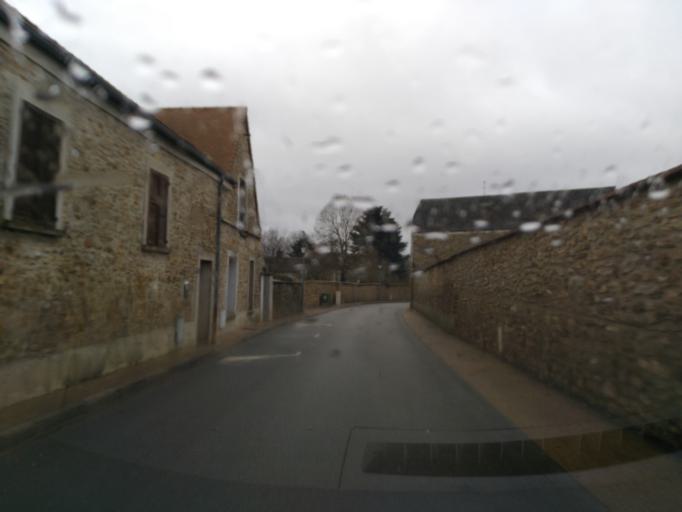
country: FR
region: Ile-de-France
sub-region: Departement des Yvelines
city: Thoiry
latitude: 48.8614
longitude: 1.8166
